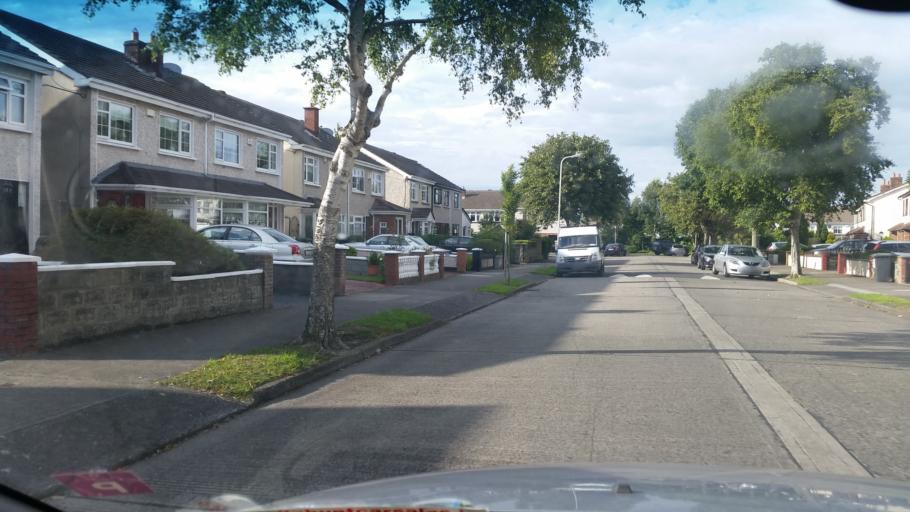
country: IE
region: Leinster
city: Donaghmede
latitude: 53.3979
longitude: -6.1713
